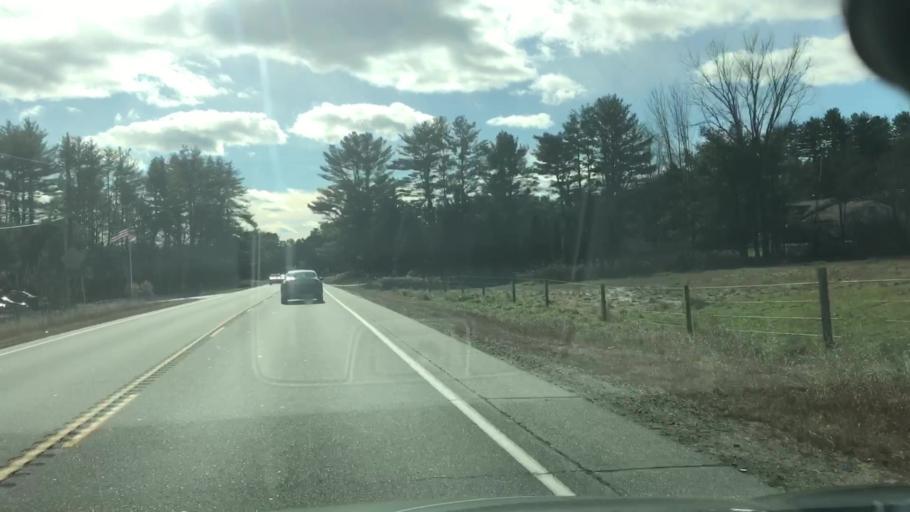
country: US
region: New Hampshire
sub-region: Merrimack County
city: Chichester
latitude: 43.2700
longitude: -71.3695
